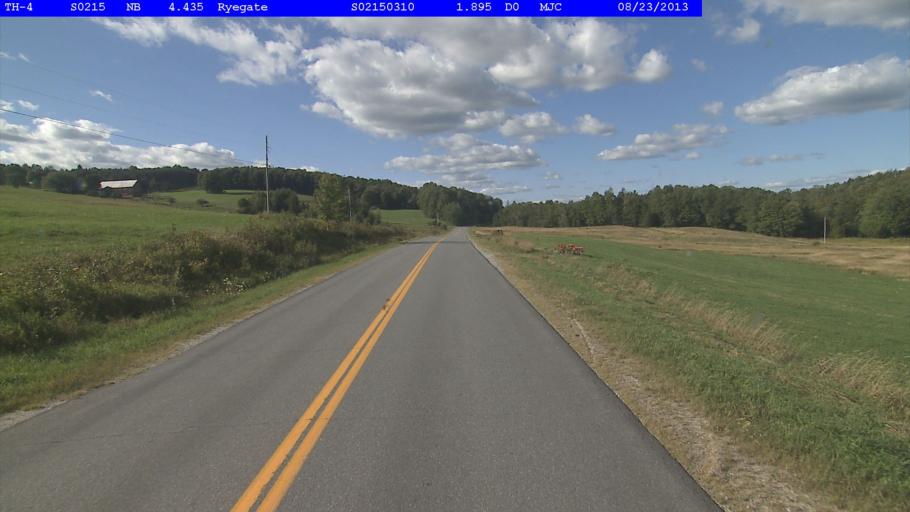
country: US
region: New Hampshire
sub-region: Grafton County
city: Woodsville
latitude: 44.2683
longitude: -72.1730
